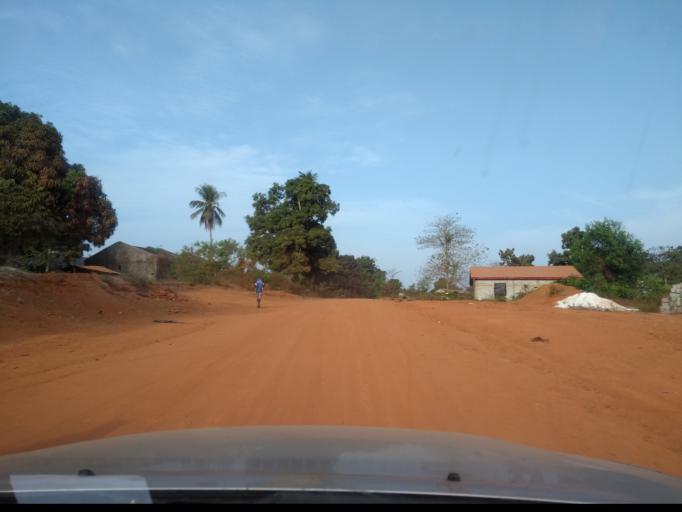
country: GN
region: Kindia
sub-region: Prefecture de Dubreka
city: Dubreka
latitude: 9.7865
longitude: -13.5396
